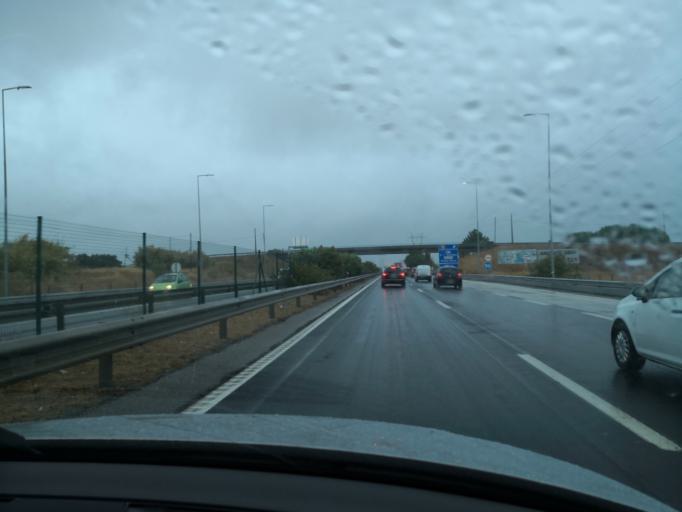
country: PT
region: Setubal
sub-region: Moita
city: Moita
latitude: 38.6654
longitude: -8.9559
